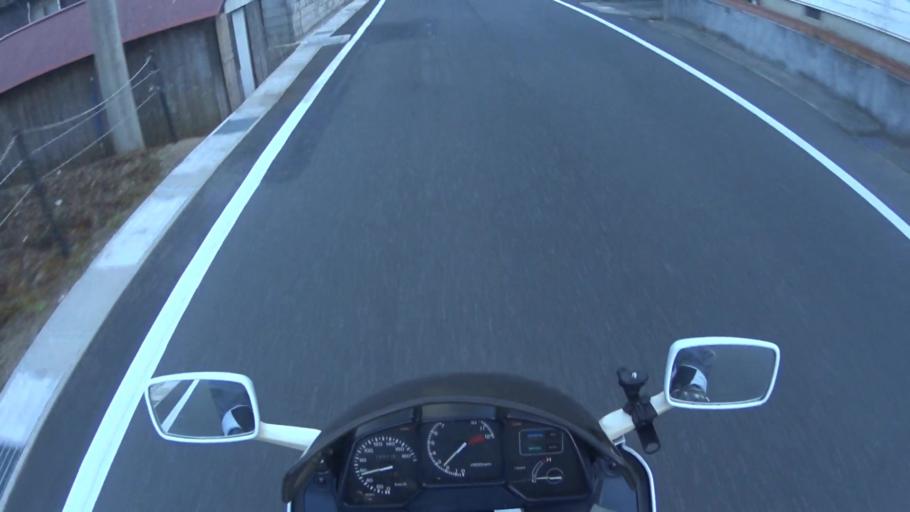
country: JP
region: Hyogo
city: Toyooka
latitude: 35.6084
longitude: 134.8918
